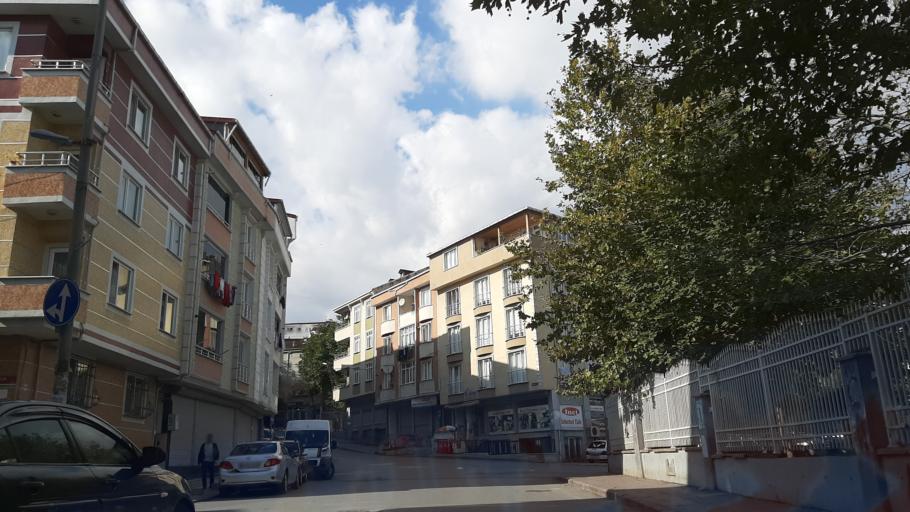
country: TR
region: Istanbul
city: Esenyurt
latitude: 41.0373
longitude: 28.6579
